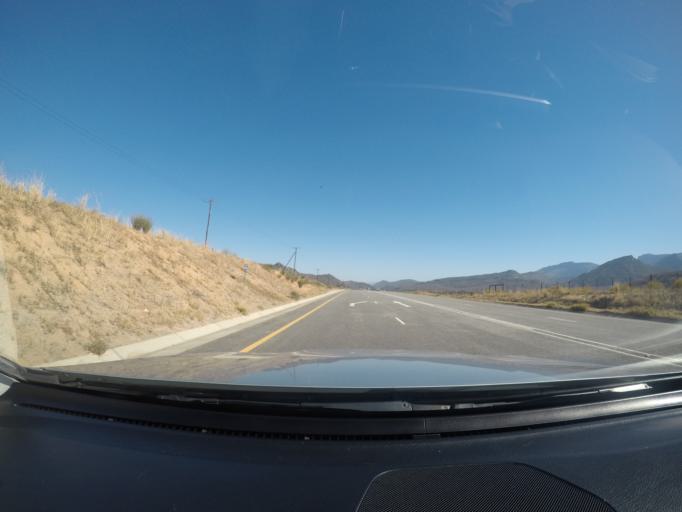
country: ZA
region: Western Cape
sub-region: West Coast District Municipality
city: Clanwilliam
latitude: -32.4667
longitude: 18.9615
